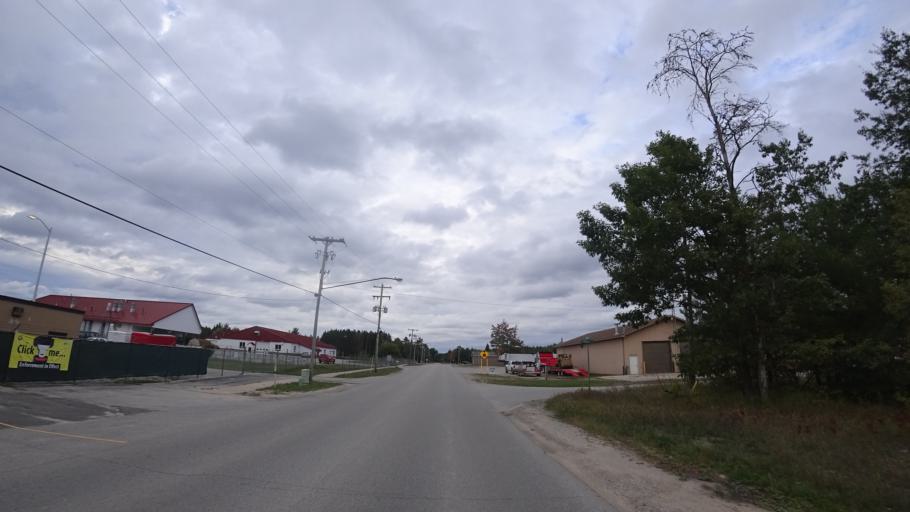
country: US
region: Michigan
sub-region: Kalkaska County
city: Kalkaska
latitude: 44.7408
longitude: -85.1845
